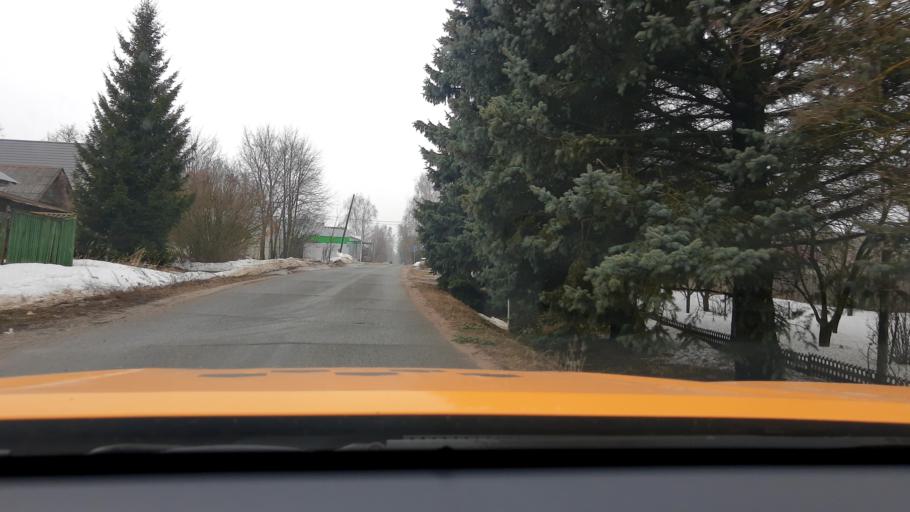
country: RU
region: Moskovskaya
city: Yamkino
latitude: 55.9168
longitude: 38.4455
